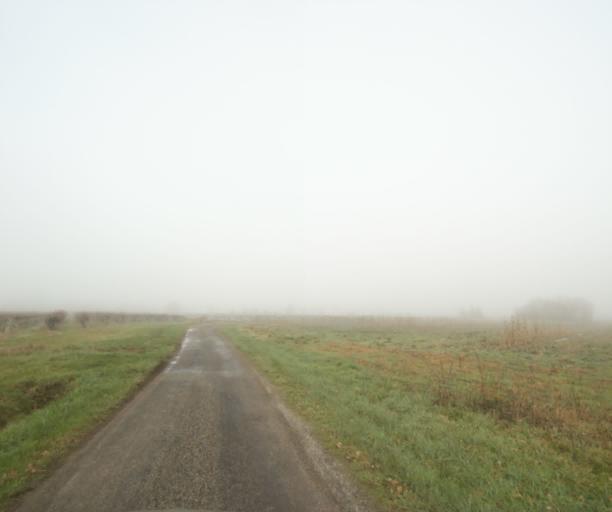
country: FR
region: Midi-Pyrenees
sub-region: Departement de la Haute-Garonne
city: Villaudric
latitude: 43.8319
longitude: 1.4598
